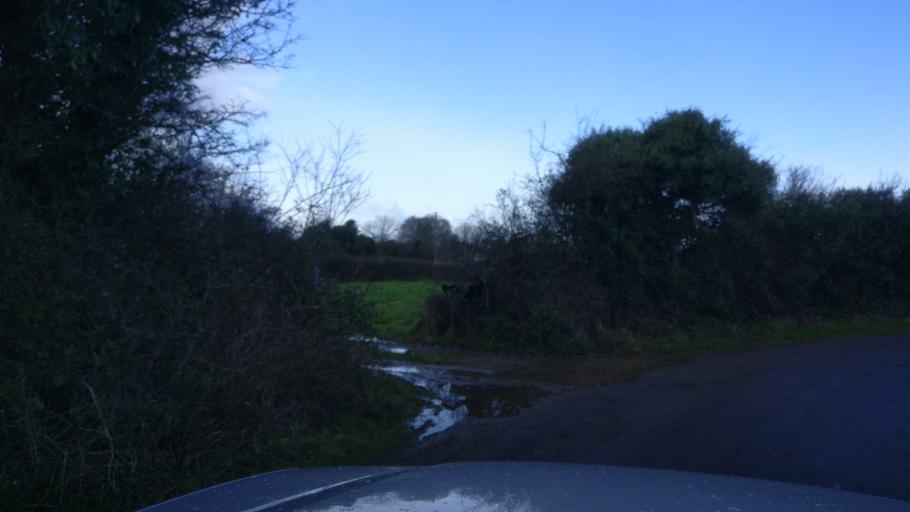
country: IE
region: Connaught
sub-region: County Galway
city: Oranmore
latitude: 53.2581
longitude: -8.8963
